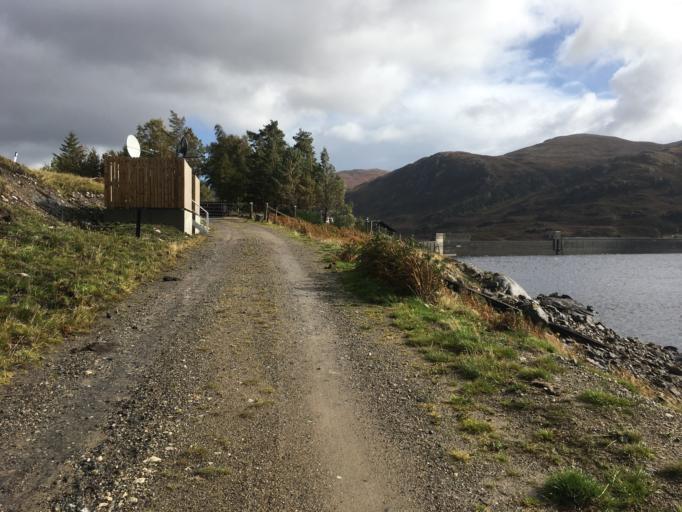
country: GB
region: Scotland
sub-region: Highland
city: Spean Bridge
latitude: 57.3397
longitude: -4.9623
